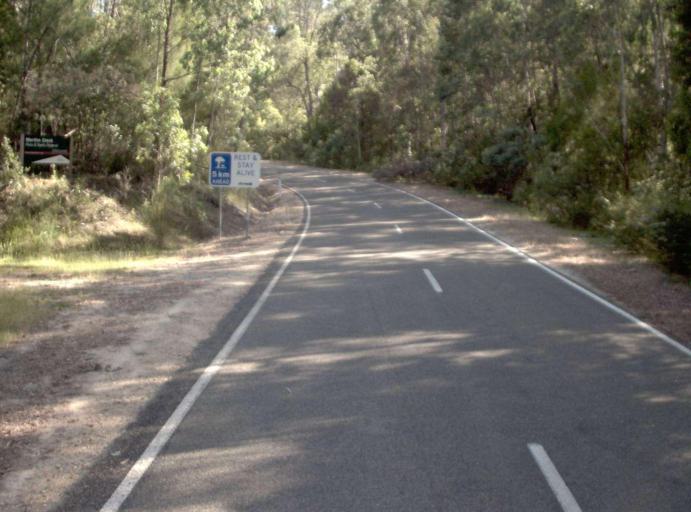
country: AU
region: Victoria
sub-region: East Gippsland
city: Lakes Entrance
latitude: -37.4863
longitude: 148.5534
